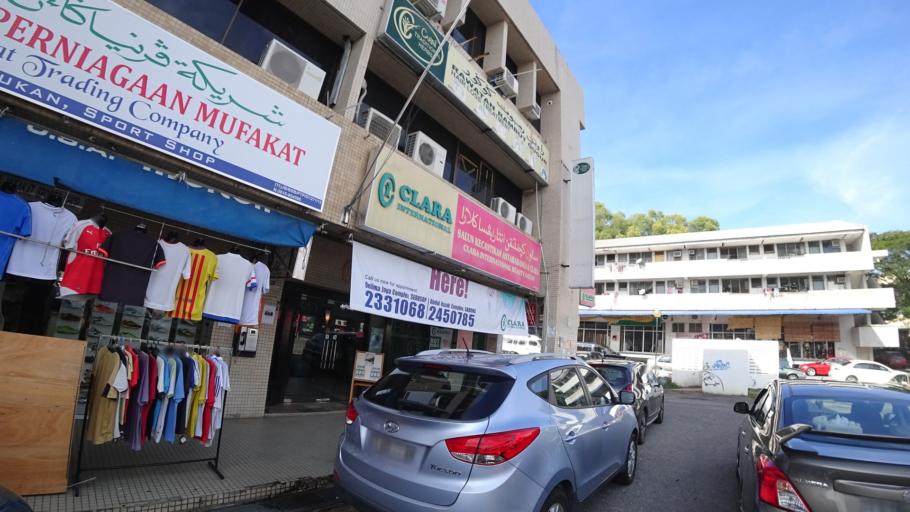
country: BN
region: Brunei and Muara
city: Bandar Seri Begawan
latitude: 4.9083
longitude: 114.9165
